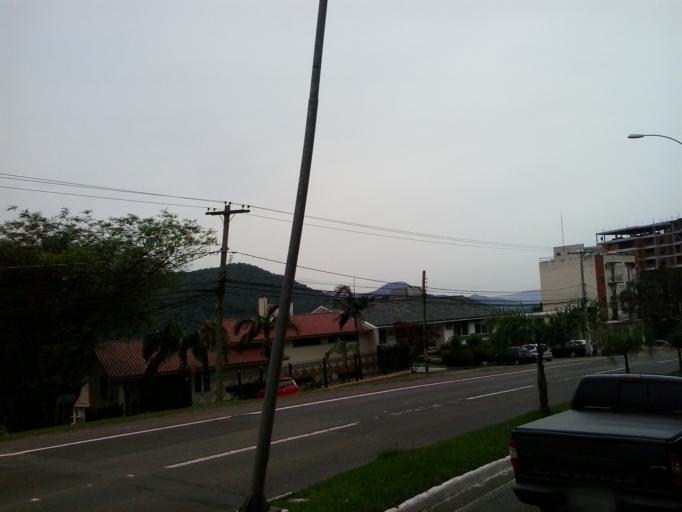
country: BR
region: Rio Grande do Sul
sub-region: Santa Maria
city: Santa Maria
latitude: -29.6925
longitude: -53.7862
